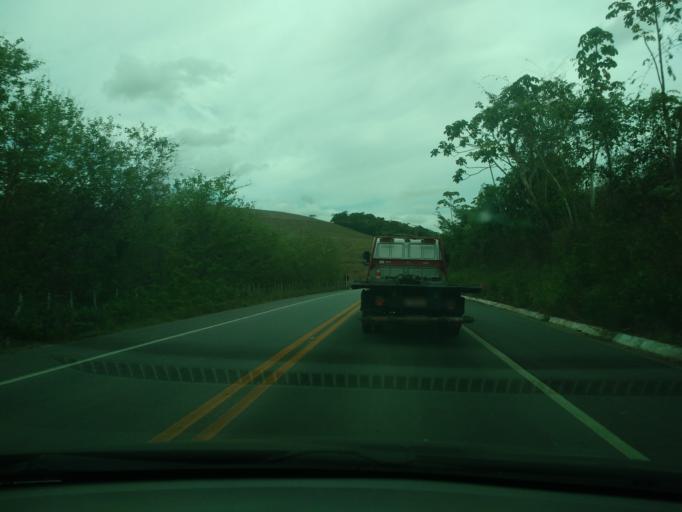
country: BR
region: Alagoas
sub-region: Murici
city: Murici
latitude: -9.3274
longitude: -35.9199
